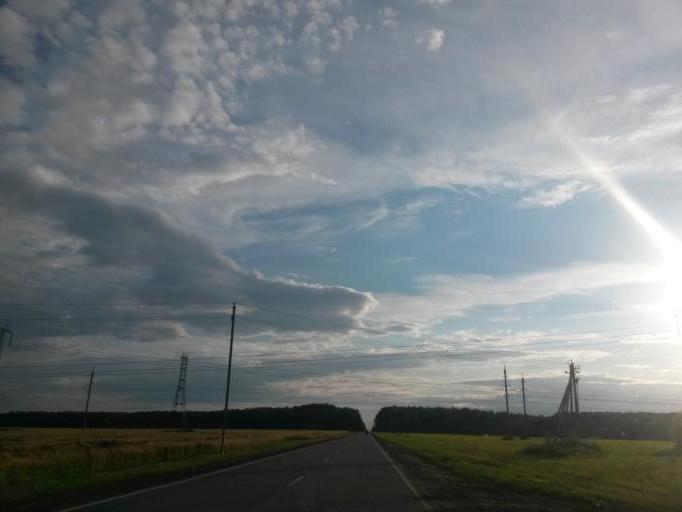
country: RU
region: Moskovskaya
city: Barybino
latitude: 55.2025
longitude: 37.8580
